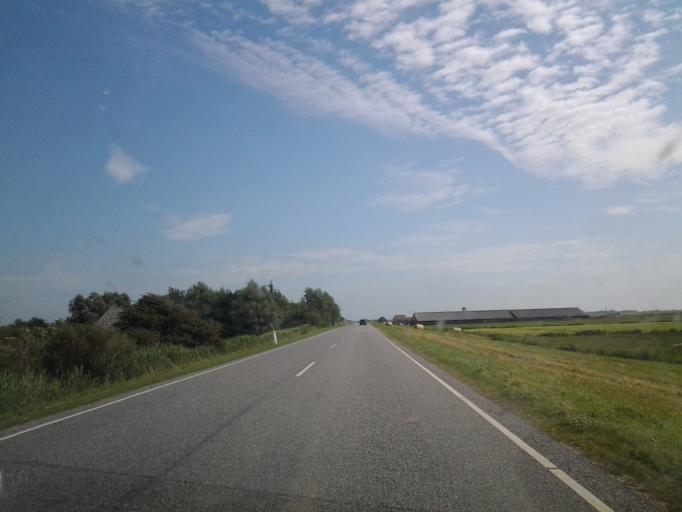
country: DE
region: Schleswig-Holstein
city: Rodenas
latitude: 54.9236
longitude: 8.7257
